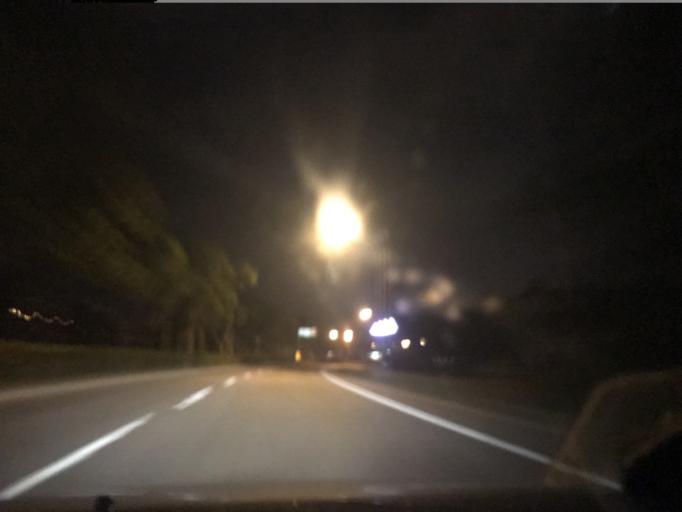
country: TW
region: Taiwan
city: Daxi
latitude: 24.8597
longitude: 121.2229
